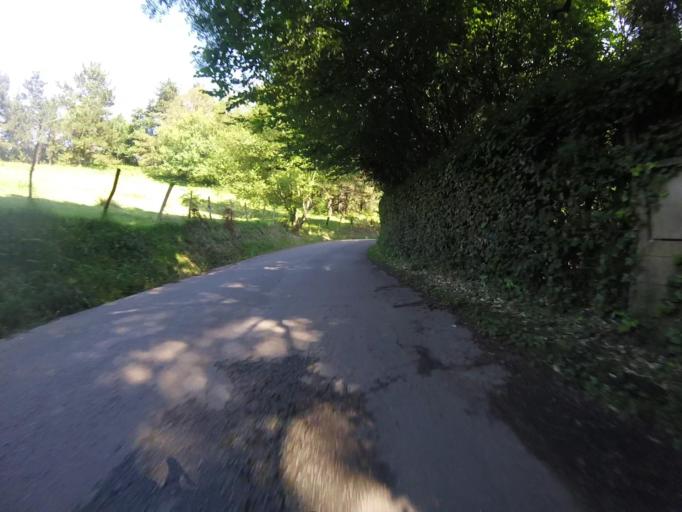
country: ES
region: Basque Country
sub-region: Provincia de Guipuzcoa
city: Astigarraga
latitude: 43.2673
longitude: -1.9301
